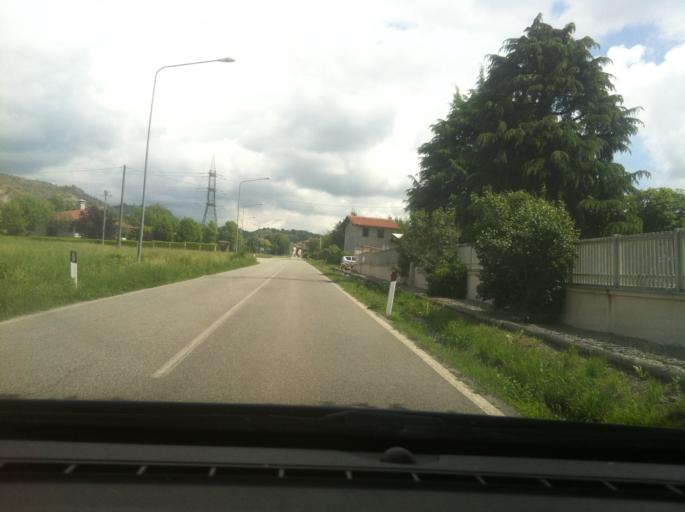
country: IT
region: Piedmont
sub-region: Provincia di Torino
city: Baldissero Canavese
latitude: 45.3983
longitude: 7.7367
